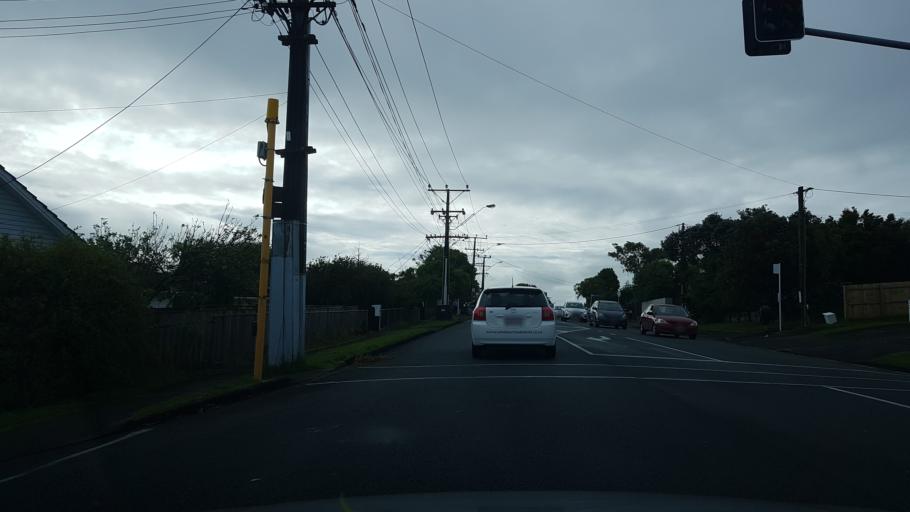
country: NZ
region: Auckland
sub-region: Auckland
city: North Shore
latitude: -36.7868
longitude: 174.7421
